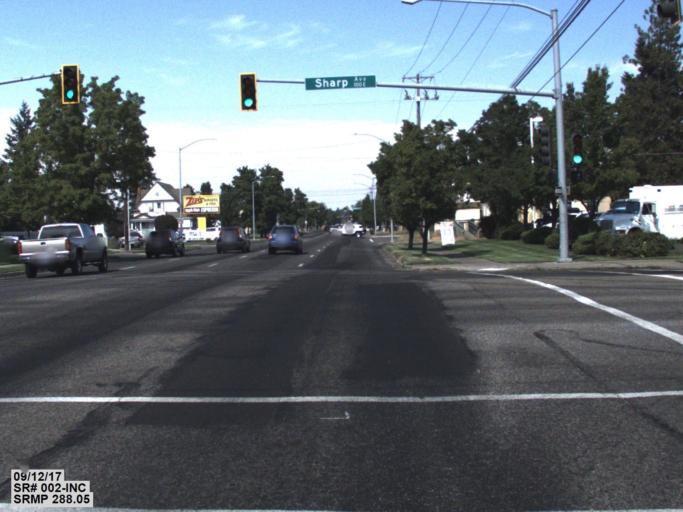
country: US
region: Washington
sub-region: Spokane County
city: Spokane
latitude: 47.6694
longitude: -117.4095
